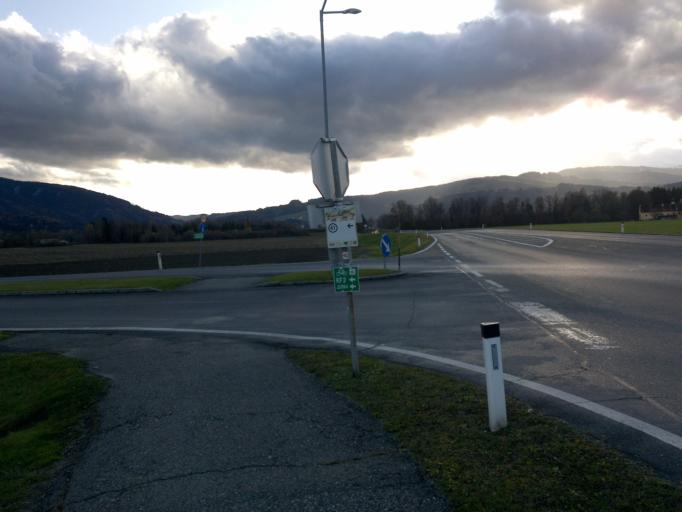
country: AT
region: Styria
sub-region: Politischer Bezirk Murtal
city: Zeltweg
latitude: 47.1799
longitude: 14.7537
